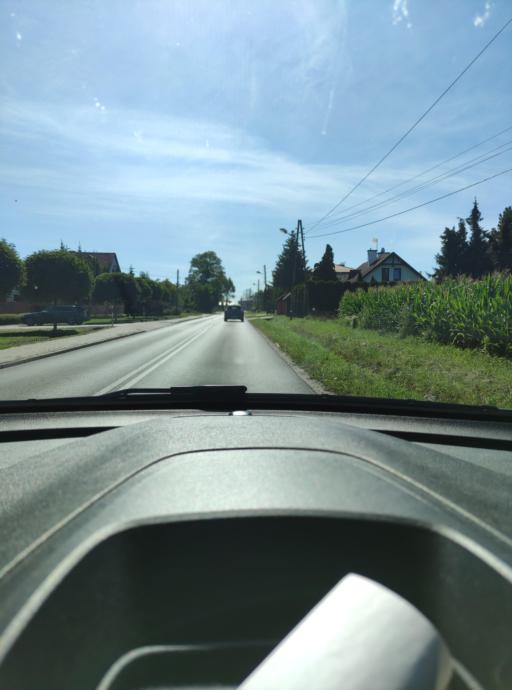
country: PL
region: Masovian Voivodeship
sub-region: Powiat pruszkowski
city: Rybie
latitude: 52.1313
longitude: 20.9245
